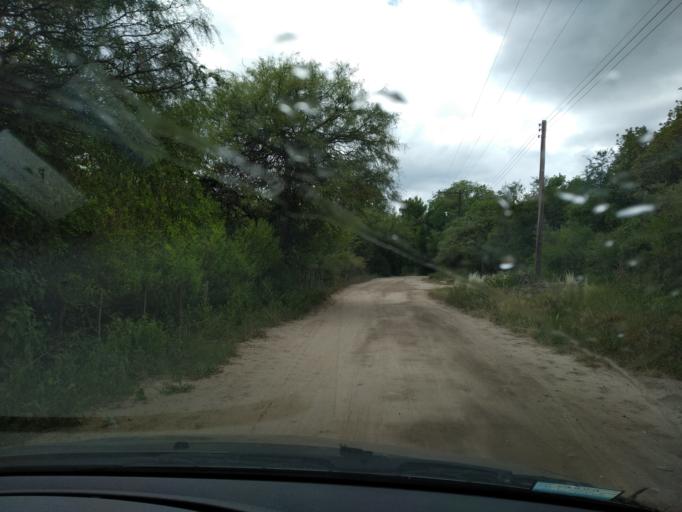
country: AR
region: Cordoba
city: Villa Las Rosas
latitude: -31.9458
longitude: -65.0359
